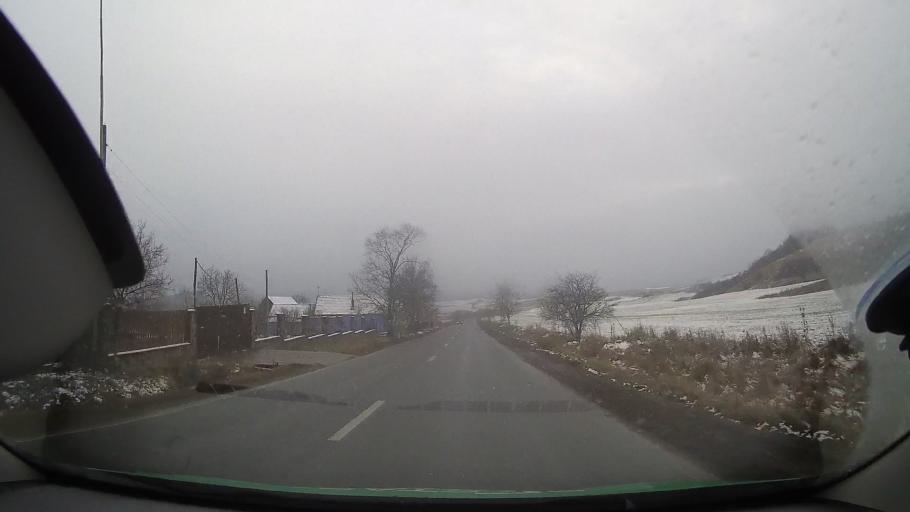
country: RO
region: Sibiu
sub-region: Comuna Blajel
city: Blajel
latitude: 46.2515
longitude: 24.2999
